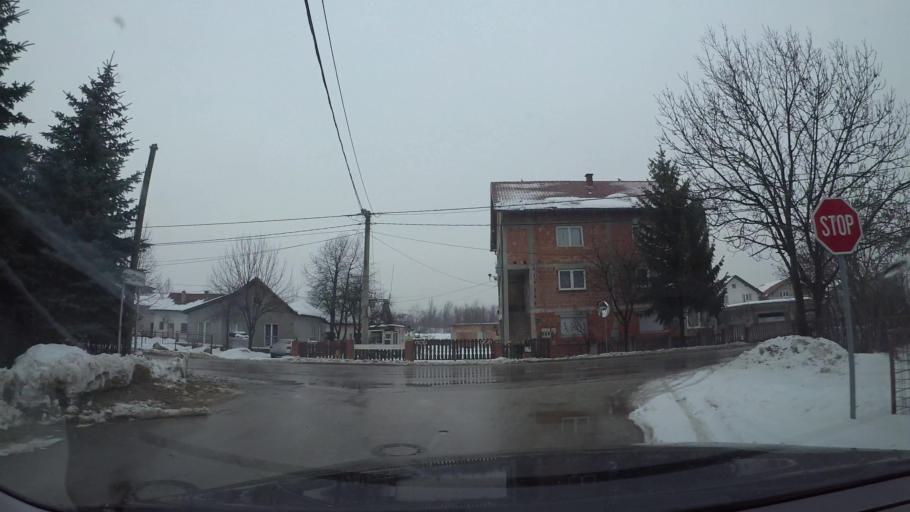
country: BA
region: Federation of Bosnia and Herzegovina
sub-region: Kanton Sarajevo
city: Sarajevo
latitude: 43.8479
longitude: 18.3134
